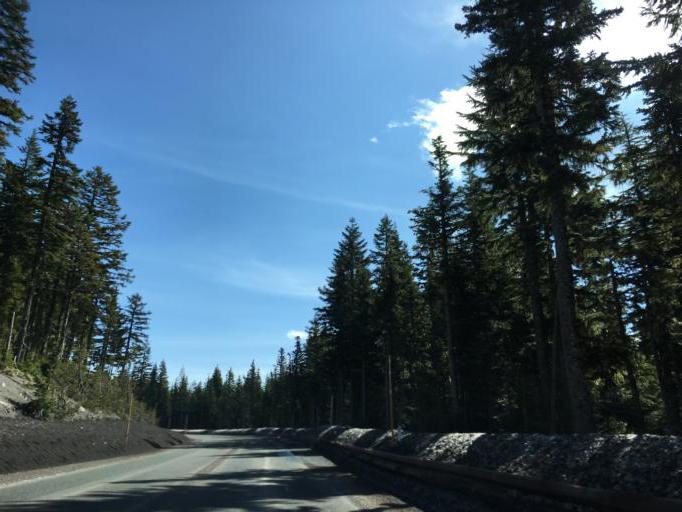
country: US
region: Oregon
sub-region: Clackamas County
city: Mount Hood Village
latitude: 45.3059
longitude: -121.7144
